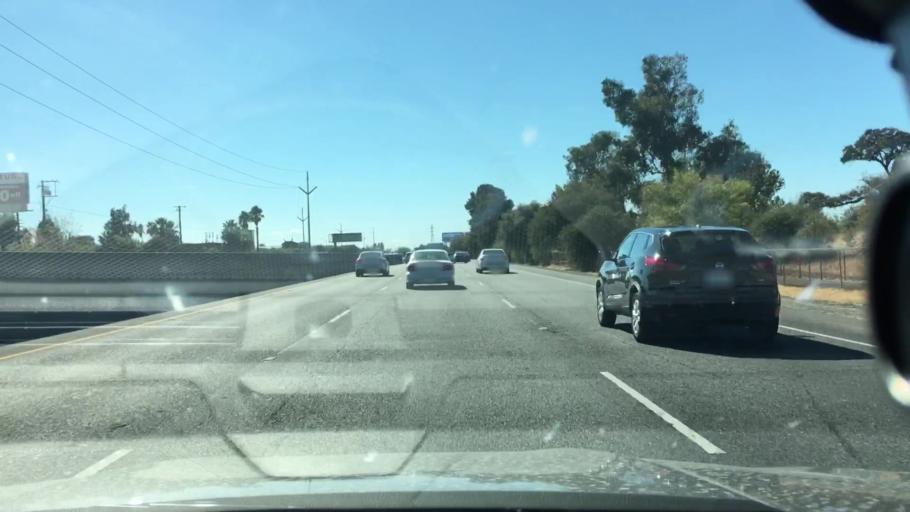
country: US
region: California
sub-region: Sacramento County
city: Arden-Arcade
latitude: 38.6281
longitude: -121.4079
